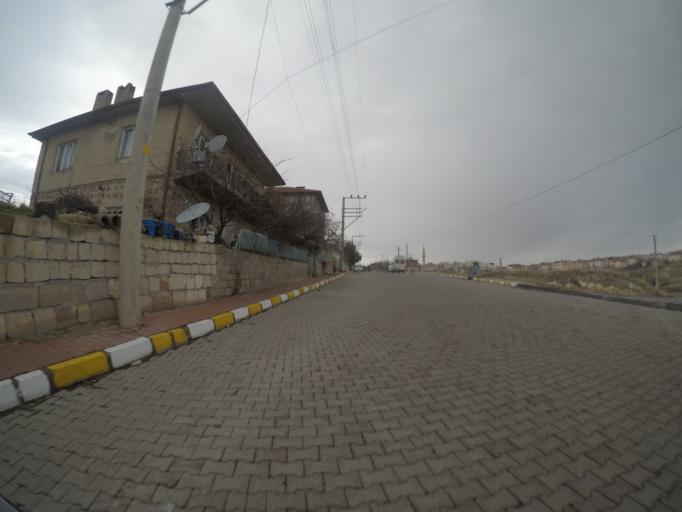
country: TR
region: Nevsehir
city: Goereme
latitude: 38.6271
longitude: 34.8598
